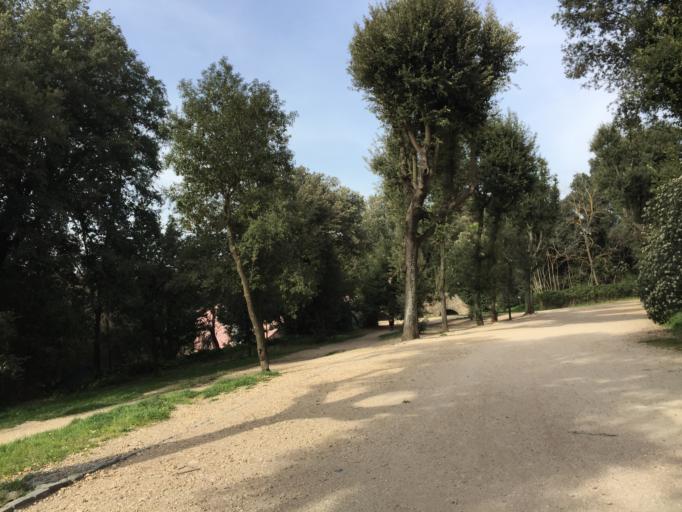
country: VA
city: Vatican City
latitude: 41.8877
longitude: 12.4541
